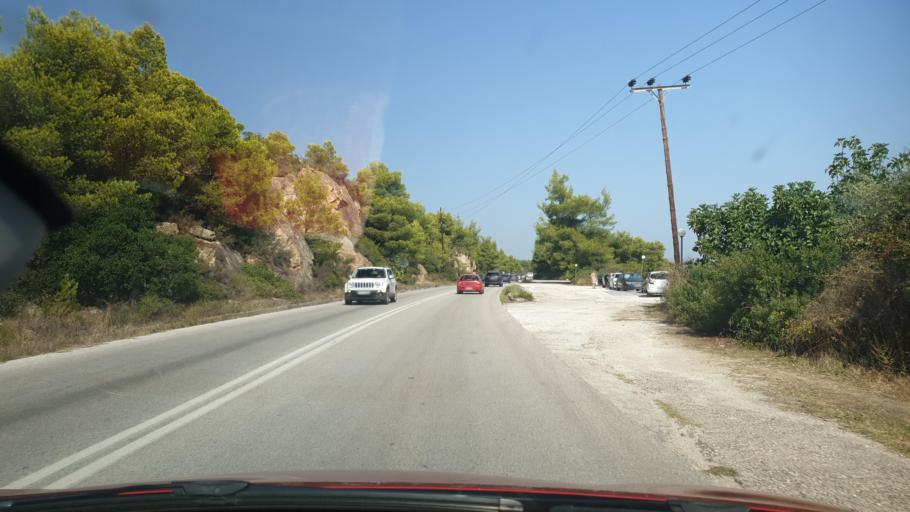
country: GR
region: Central Macedonia
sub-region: Nomos Chalkidikis
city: Agios Nikolaos
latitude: 40.2294
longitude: 23.7371
